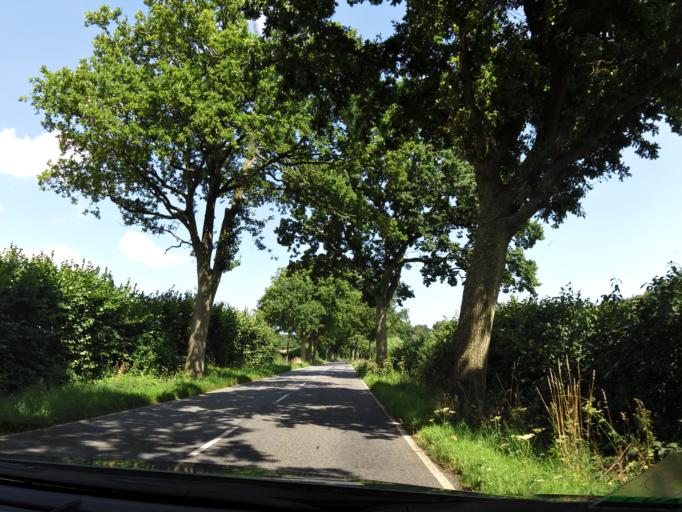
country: DK
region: South Denmark
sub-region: Assens Kommune
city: Arup
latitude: 55.4016
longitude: 10.0469
